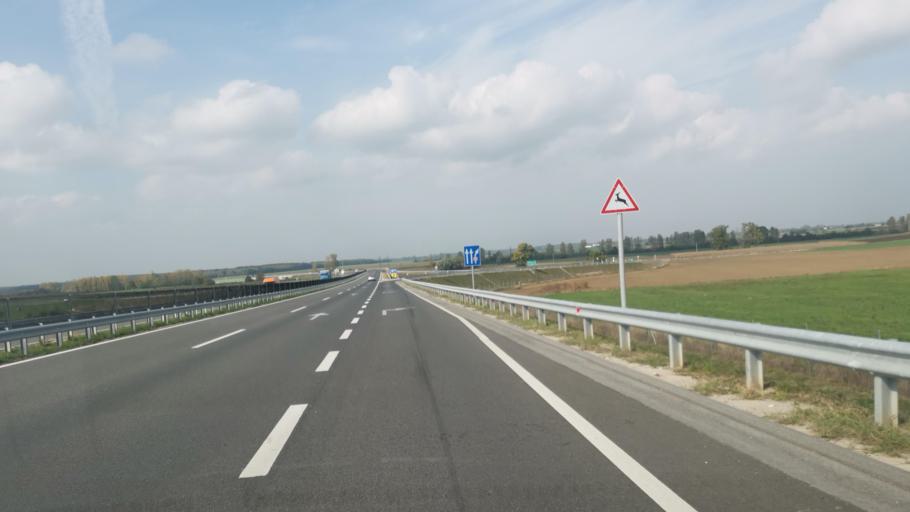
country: HU
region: Gyor-Moson-Sopron
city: Fertoszentmiklos
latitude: 47.5630
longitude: 16.8628
